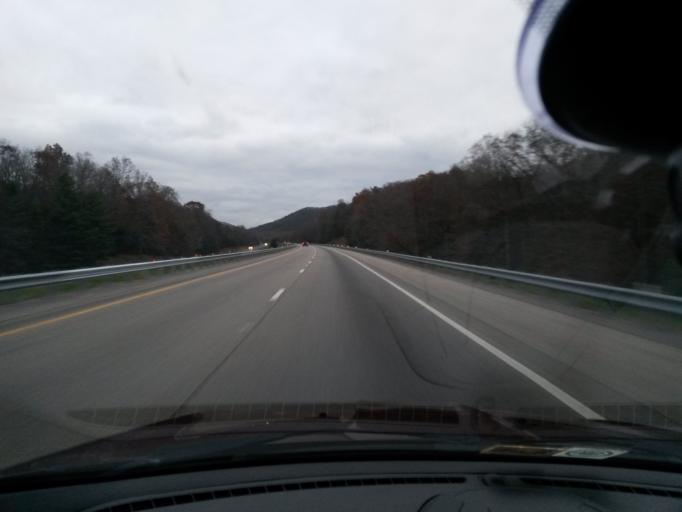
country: US
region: Virginia
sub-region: Alleghany County
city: Clifton Forge
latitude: 37.8398
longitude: -79.6420
